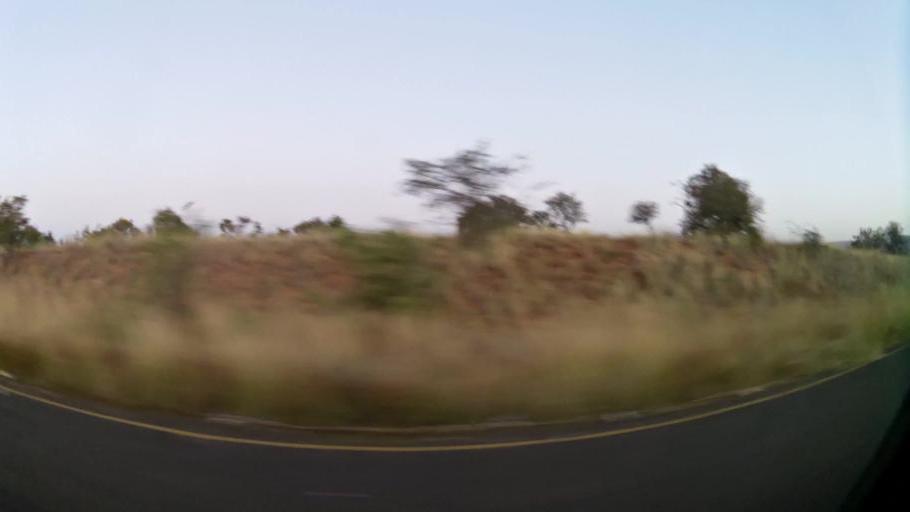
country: ZA
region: North-West
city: Ga-Rankuwa
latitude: -25.6364
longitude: 27.9530
